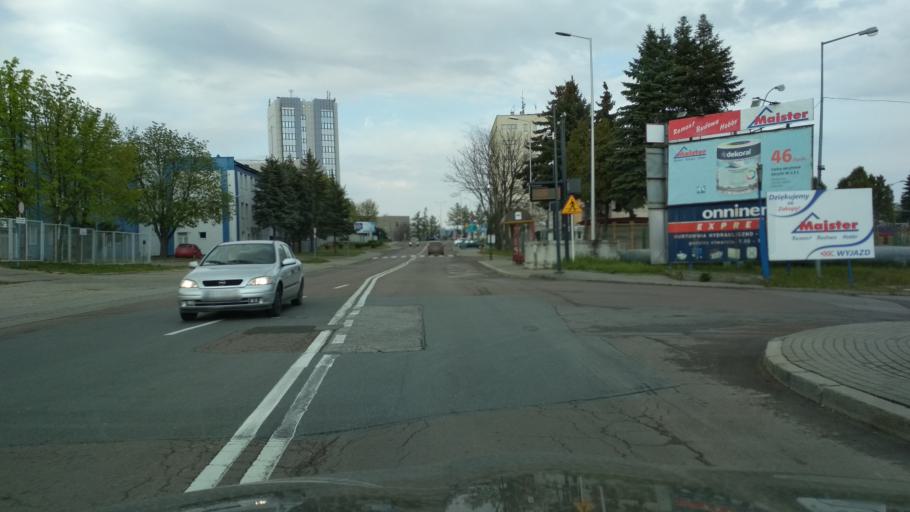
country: PL
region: Subcarpathian Voivodeship
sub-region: Rzeszow
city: Rzeszow
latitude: 50.0255
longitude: 21.9739
